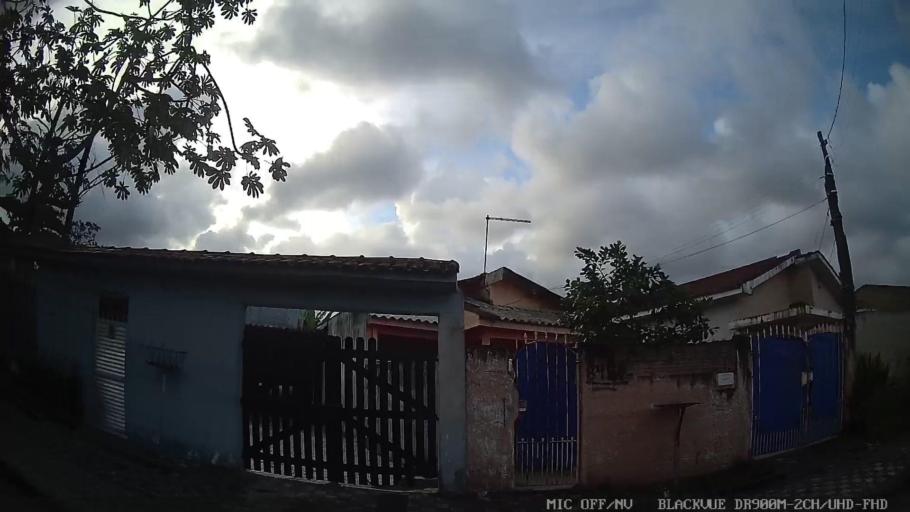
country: BR
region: Sao Paulo
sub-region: Mongagua
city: Mongagua
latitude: -24.1188
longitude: -46.6753
